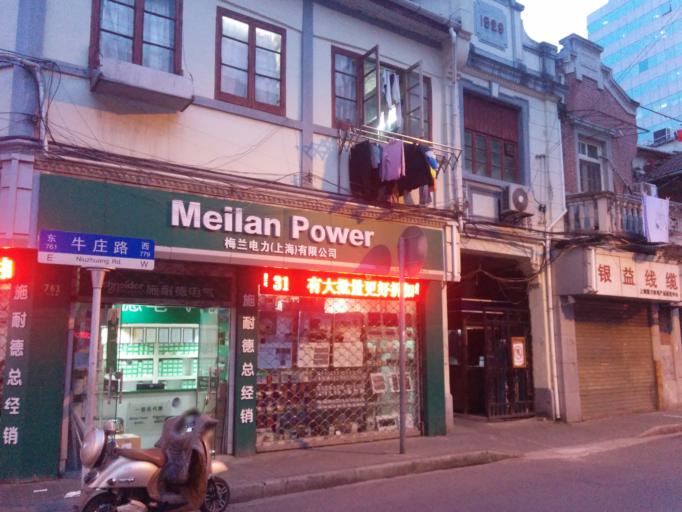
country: CN
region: Shanghai Shi
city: Hongkou
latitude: 31.2392
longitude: 121.4712
